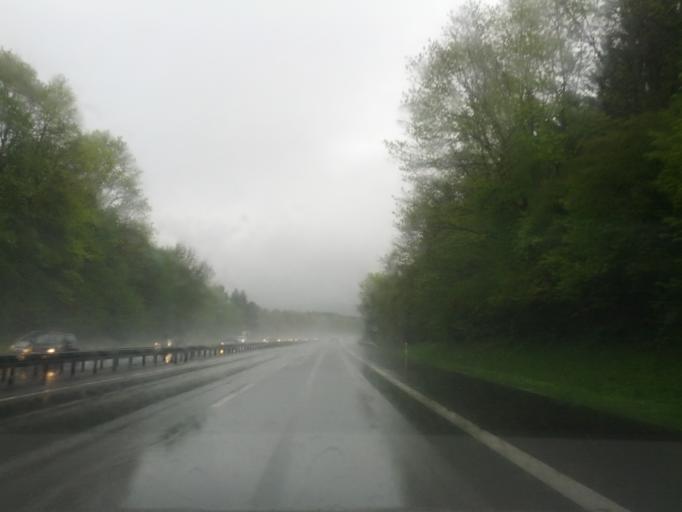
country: DE
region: North Rhine-Westphalia
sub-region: Regierungsbezirk Koln
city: Overath
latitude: 50.9574
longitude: 7.3230
